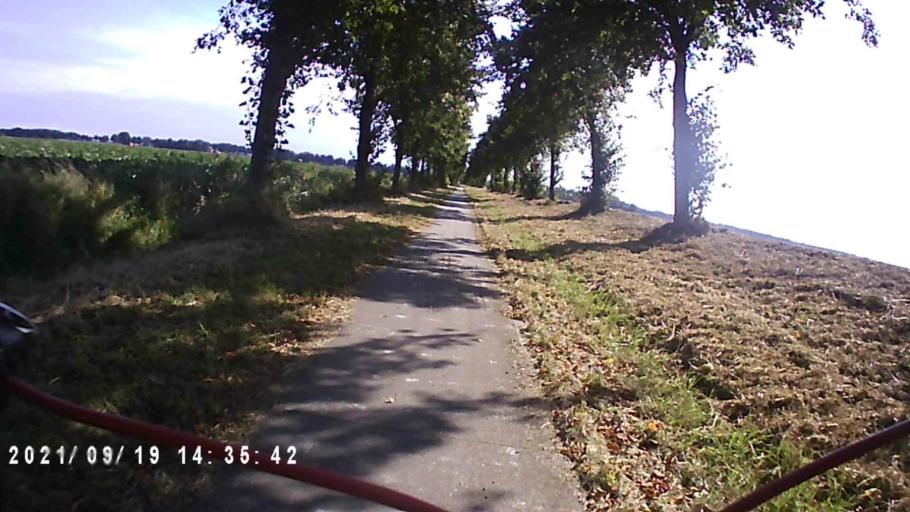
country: NL
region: Groningen
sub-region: Gemeente  Oldambt
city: Winschoten
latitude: 53.1366
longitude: 7.1518
